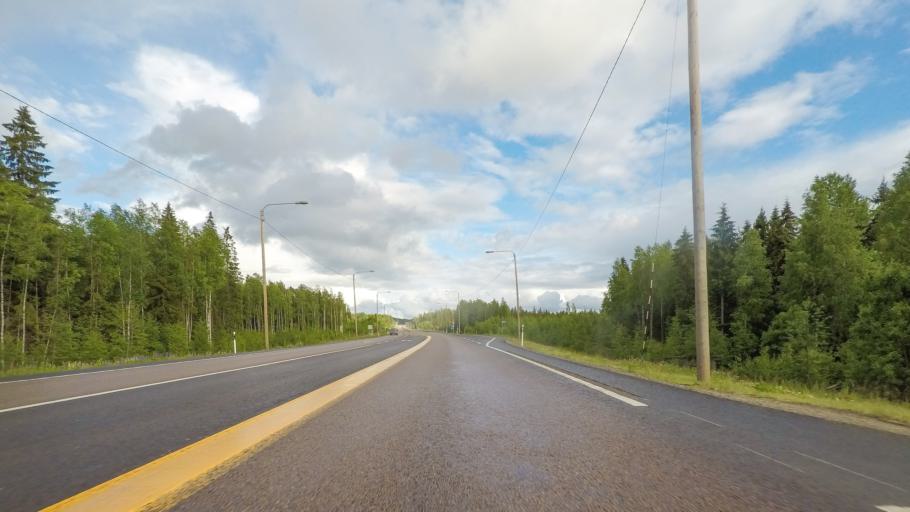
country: FI
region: Paijanne Tavastia
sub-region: Lahti
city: Hartola
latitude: 61.4268
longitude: 26.0136
